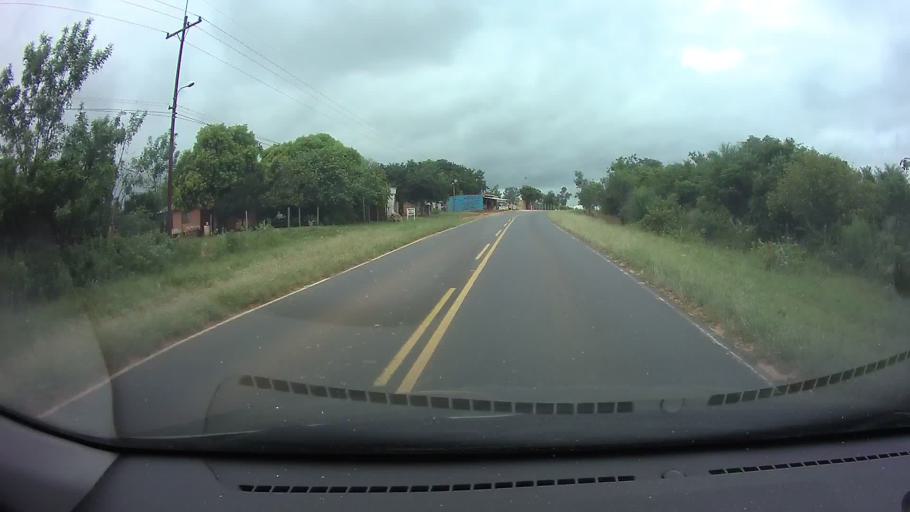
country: PY
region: Central
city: Guarambare
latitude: -25.5180
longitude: -57.4907
